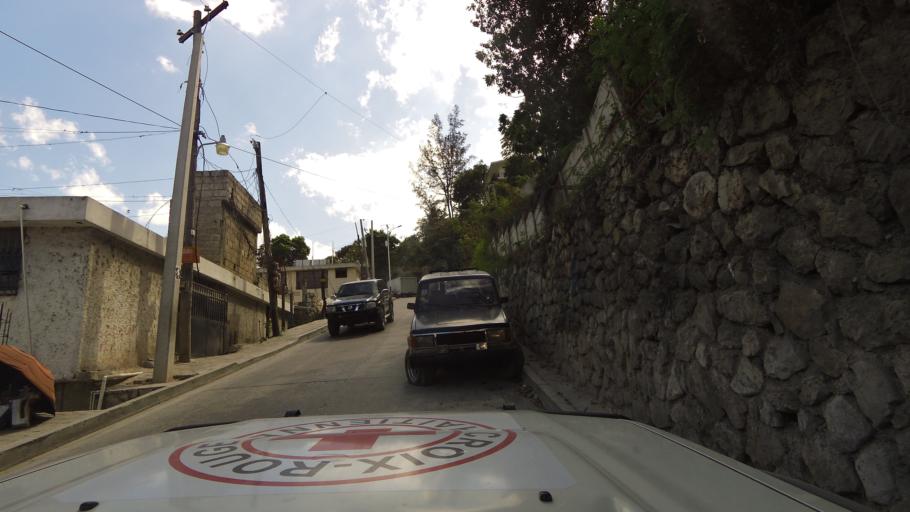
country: HT
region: Ouest
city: Petionville
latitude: 18.5273
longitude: -72.2921
